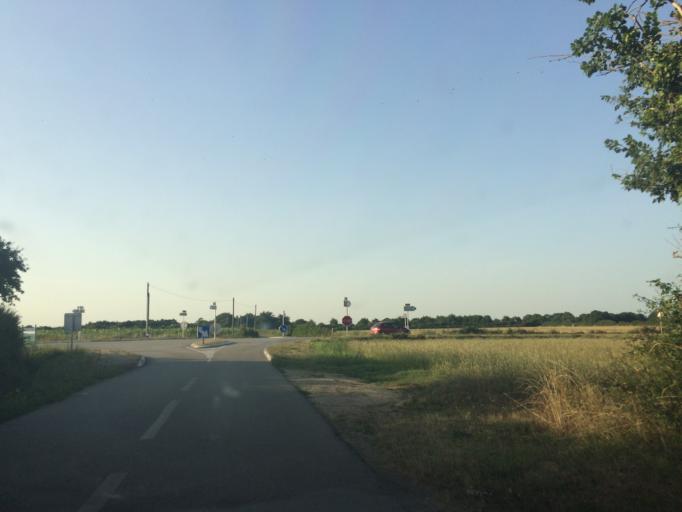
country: FR
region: Brittany
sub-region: Departement du Morbihan
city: Ambon
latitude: 47.5310
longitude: -2.5547
